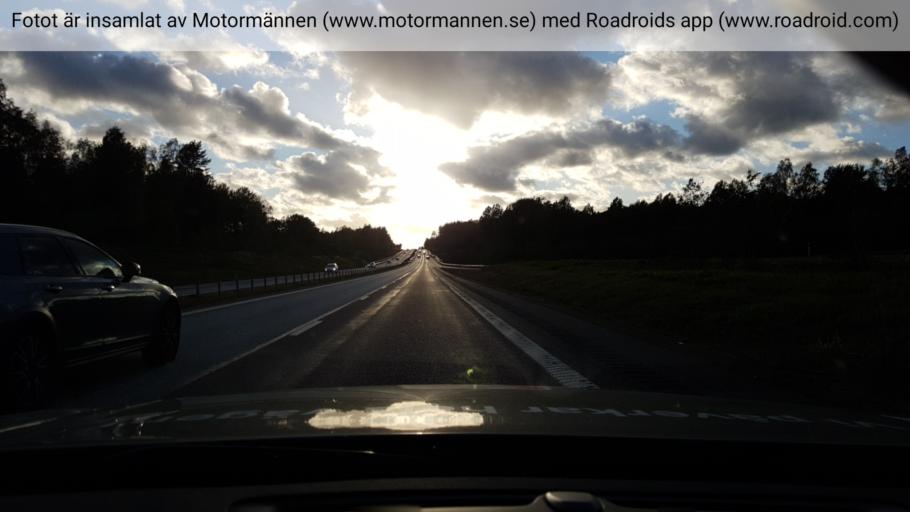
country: SE
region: Vaermland
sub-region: Karlstads Kommun
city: Skattkarr
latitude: 59.4023
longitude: 13.6138
